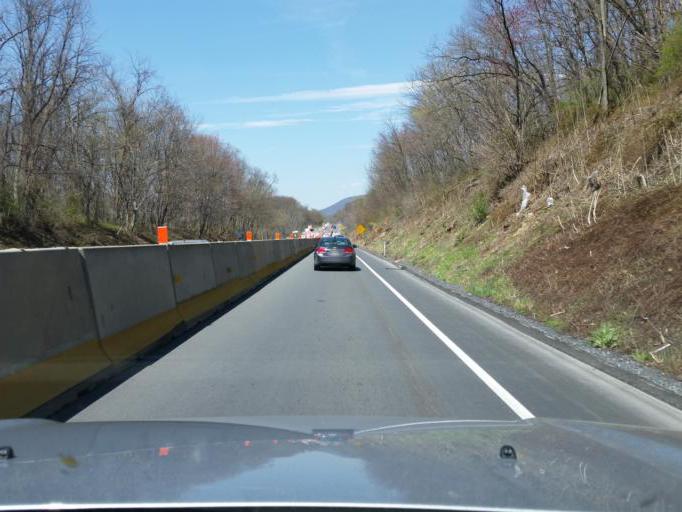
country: US
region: Pennsylvania
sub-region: Mifflin County
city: Lewistown
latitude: 40.5823
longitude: -77.5543
